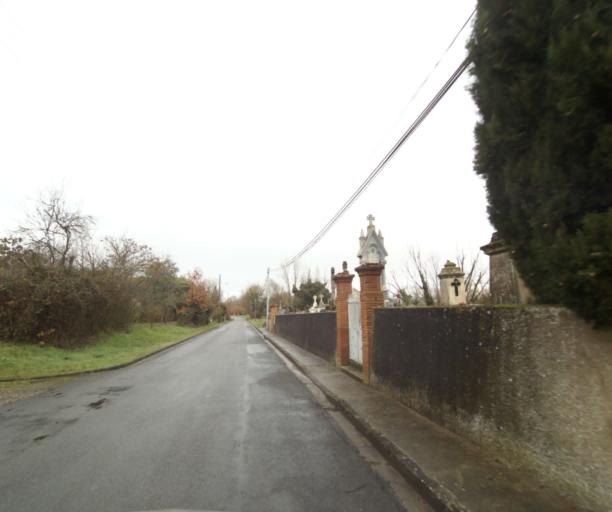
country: FR
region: Midi-Pyrenees
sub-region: Departement du Tarn-et-Garonne
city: Nohic
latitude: 43.8720
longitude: 1.4671
